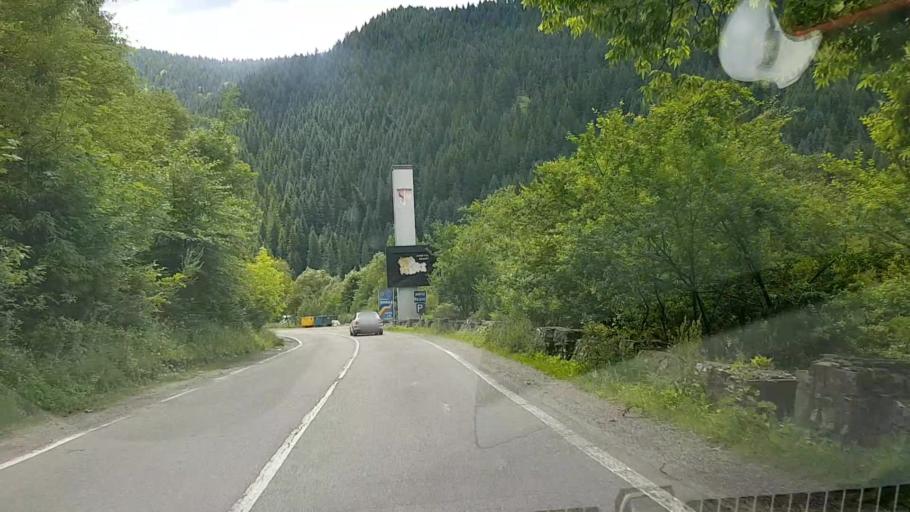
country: RO
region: Suceava
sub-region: Comuna Brosteni
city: Brosteni
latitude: 47.2202
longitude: 25.7385
